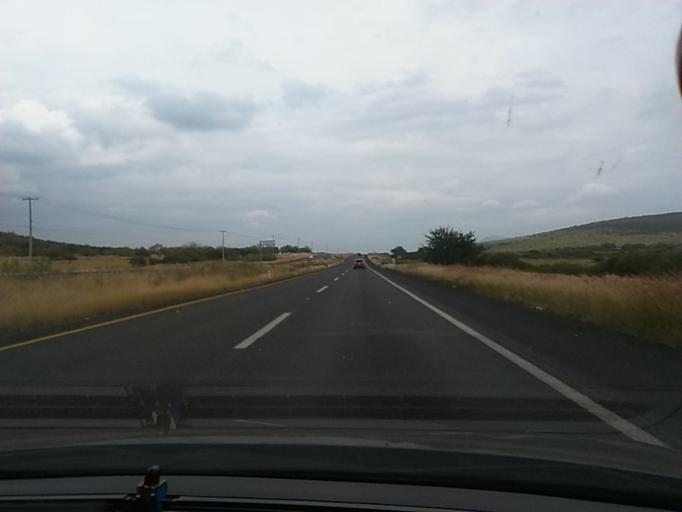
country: MX
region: Michoacan
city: Ecuandureo
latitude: 20.1742
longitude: -102.1707
